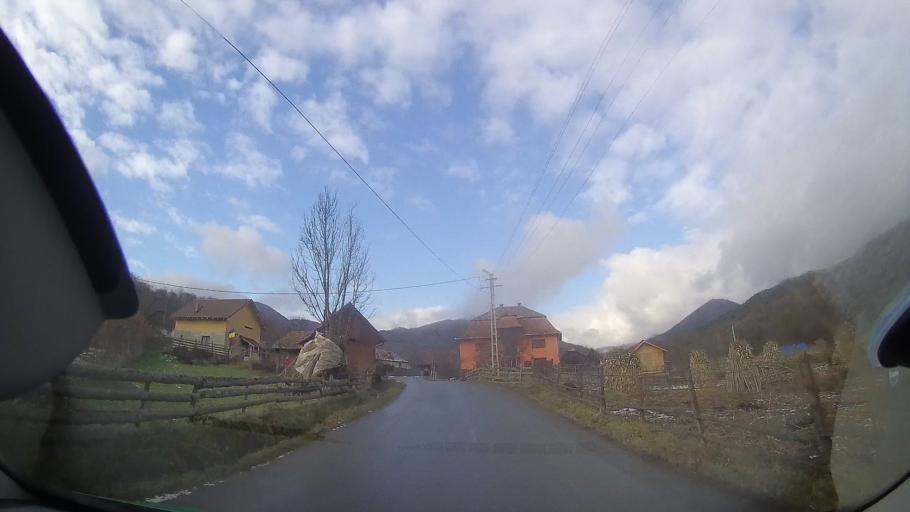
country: RO
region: Alba
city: Salciua de Sus
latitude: 46.4278
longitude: 23.4448
